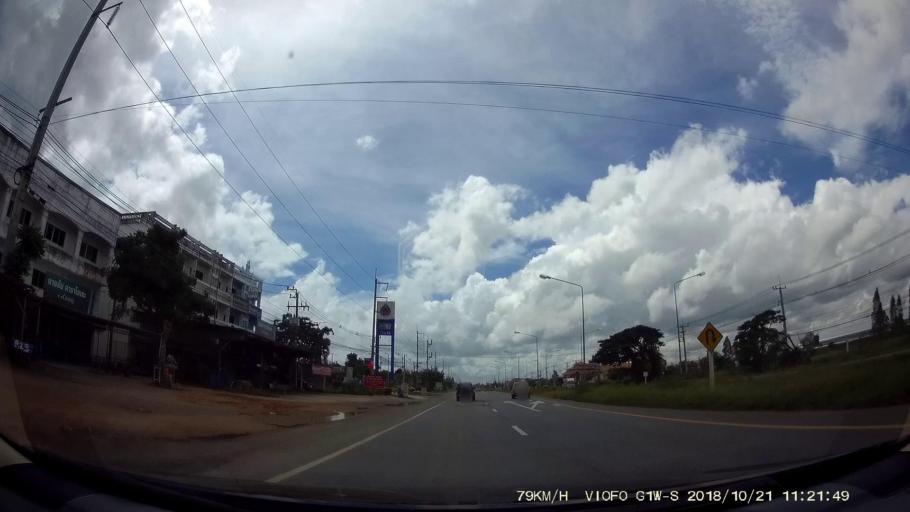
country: TH
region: Chaiyaphum
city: Chaiyaphum
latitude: 15.8424
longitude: 102.0628
